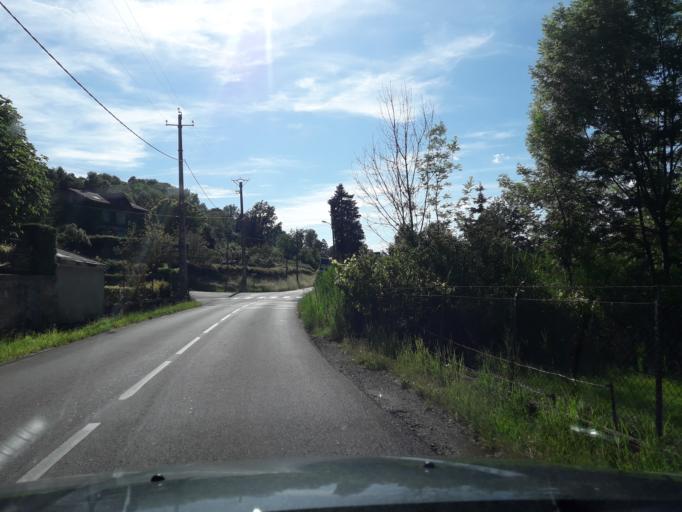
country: FR
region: Rhone-Alpes
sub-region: Departement de la Savoie
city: La Bridoire
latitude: 45.5382
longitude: 5.7931
